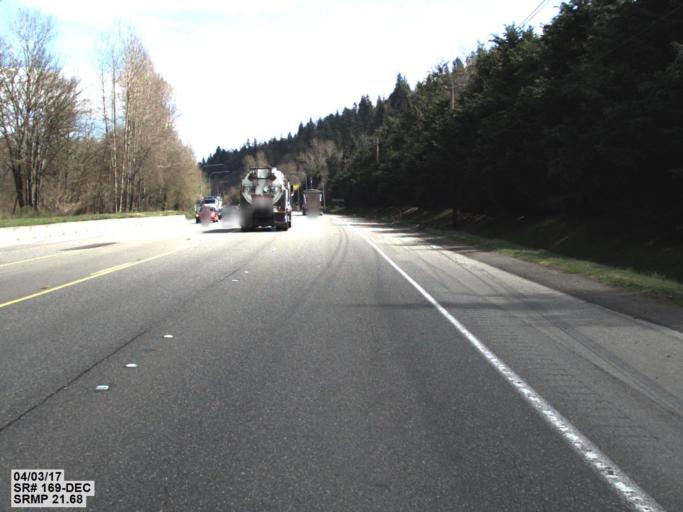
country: US
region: Washington
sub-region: King County
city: East Renton Highlands
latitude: 47.4639
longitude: -122.1293
